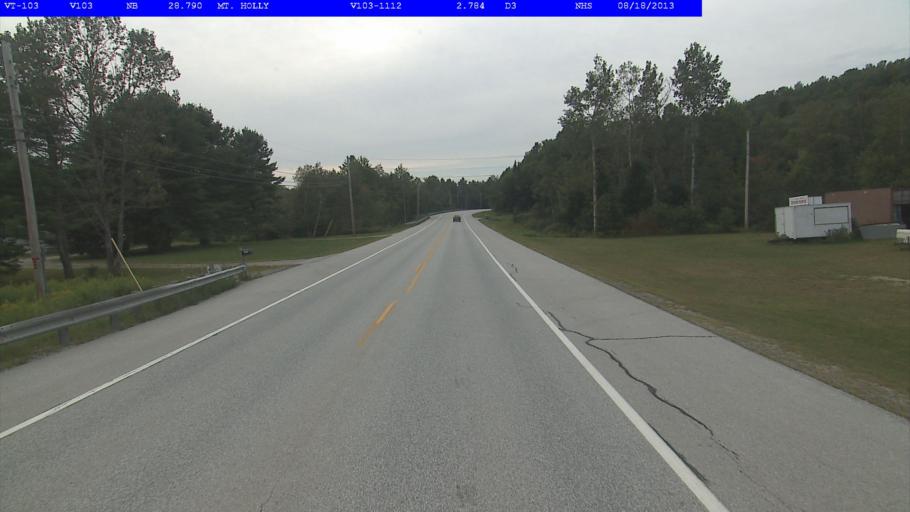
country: US
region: Vermont
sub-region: Rutland County
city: Rutland
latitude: 43.4499
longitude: -72.7822
